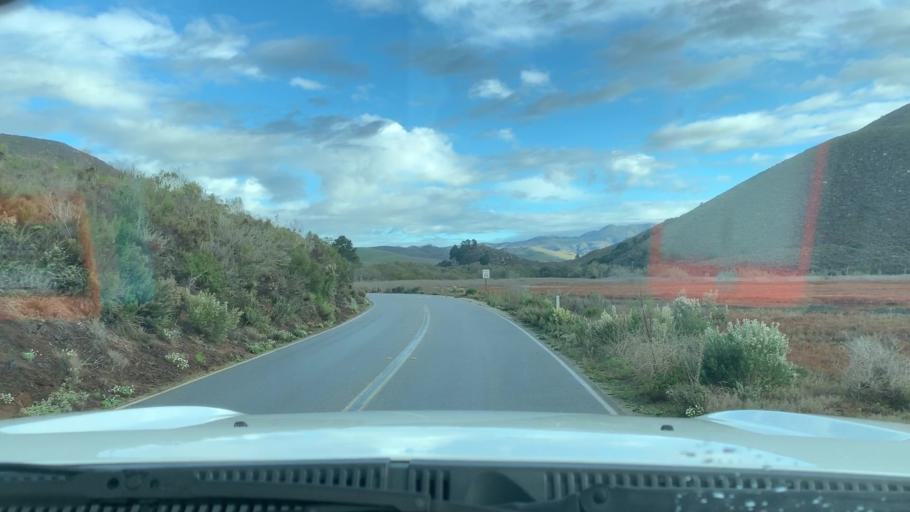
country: US
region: California
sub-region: San Luis Obispo County
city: Morro Bay
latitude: 35.3482
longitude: -120.8339
